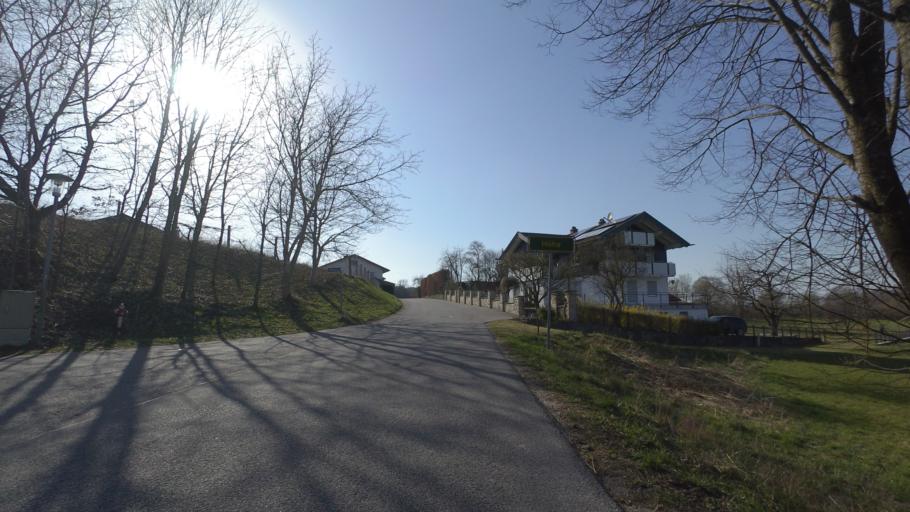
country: DE
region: Bavaria
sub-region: Upper Bavaria
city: Traunreut
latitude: 47.9406
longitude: 12.5887
